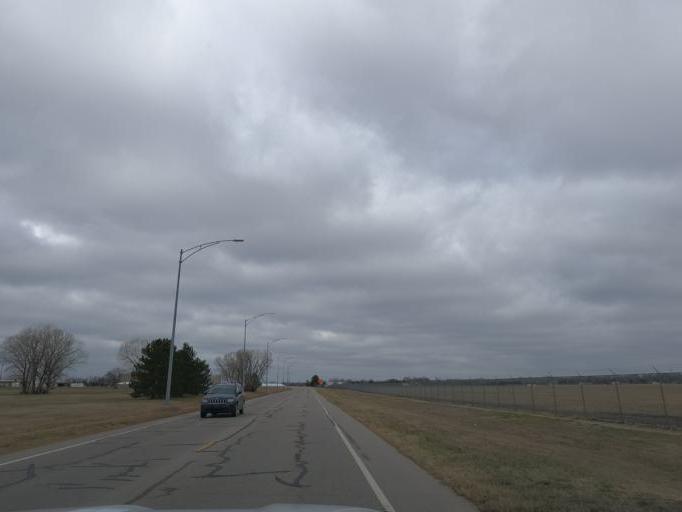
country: US
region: Kansas
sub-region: Reno County
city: Hutchinson
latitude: 38.0683
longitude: -97.8738
